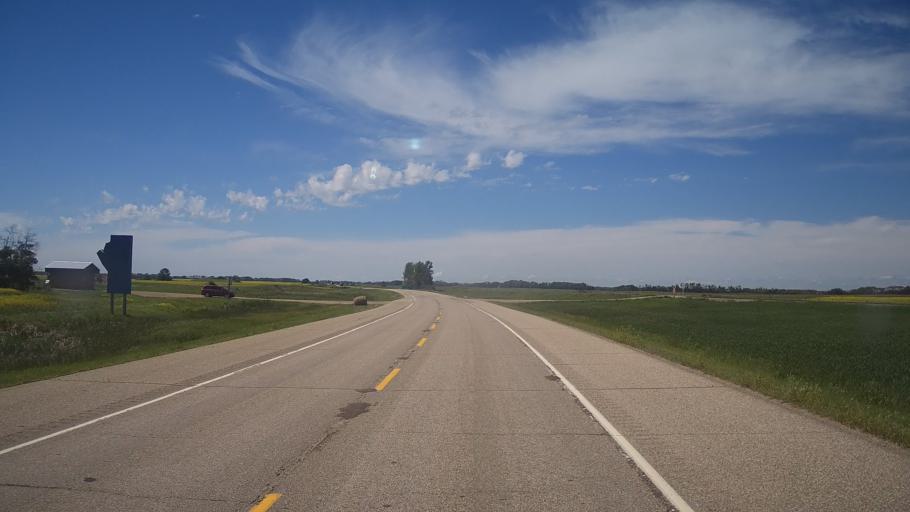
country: CA
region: Saskatchewan
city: Langenburg
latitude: 50.7762
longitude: -101.5072
